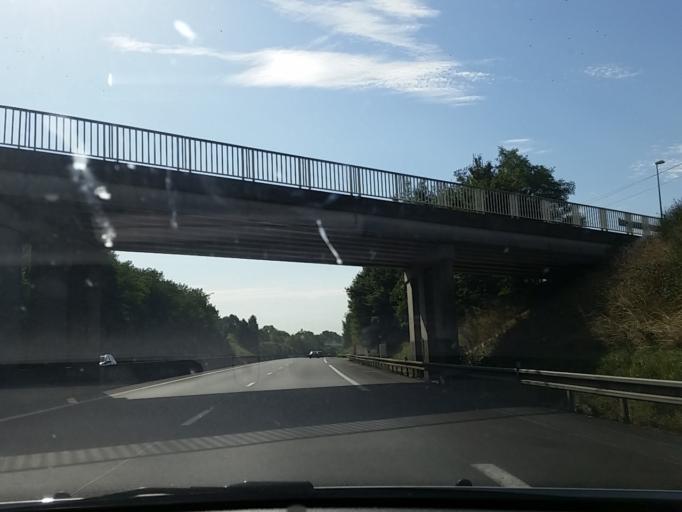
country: FR
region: Centre
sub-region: Departement du Cher
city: Vierzon
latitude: 47.2331
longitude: 2.0963
